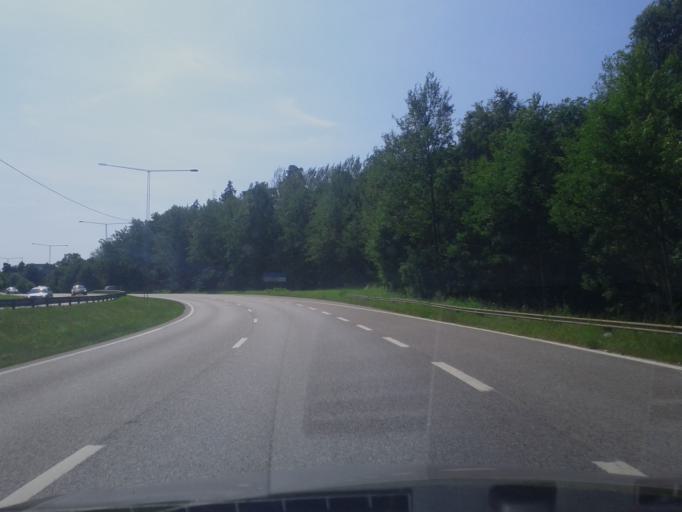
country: SE
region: Stockholm
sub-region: Huddinge Kommun
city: Huddinge
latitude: 59.2666
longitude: 18.0052
